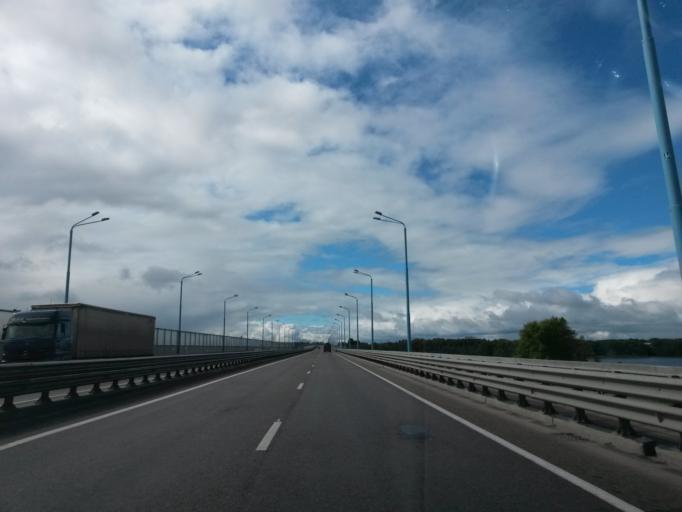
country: RU
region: Jaroslavl
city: Yaroslavl
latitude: 57.6779
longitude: 39.8653
